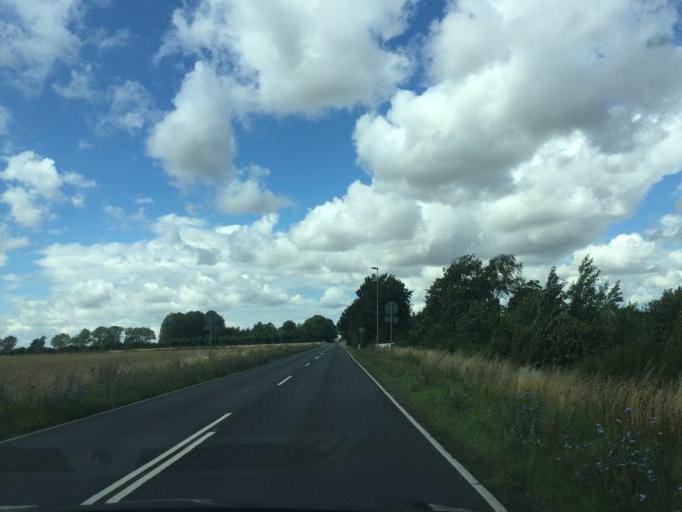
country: DK
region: South Denmark
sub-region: Odense Kommune
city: Stige
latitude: 55.4548
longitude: 10.3673
